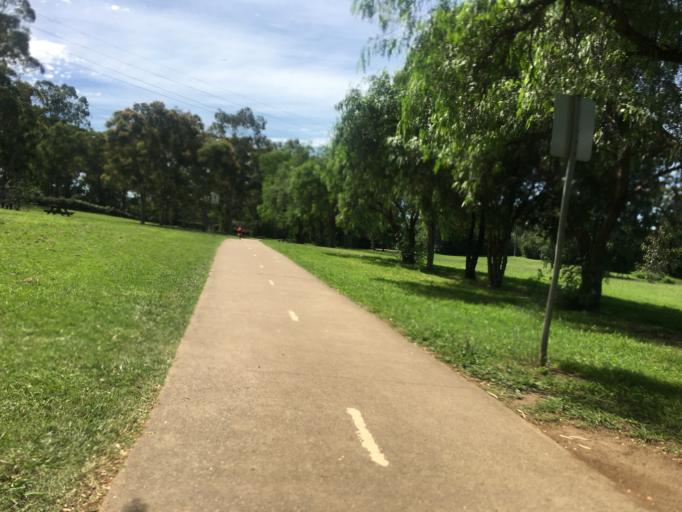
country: AU
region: New South Wales
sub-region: Camden
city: Camden South
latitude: -34.0779
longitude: 150.7007
